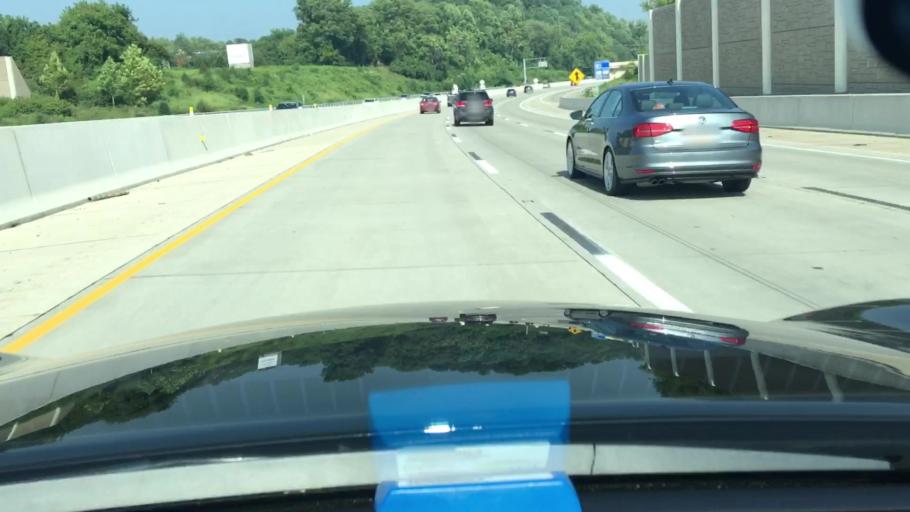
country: US
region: Pennsylvania
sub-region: Chester County
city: Malvern
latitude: 40.0517
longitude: -75.5610
